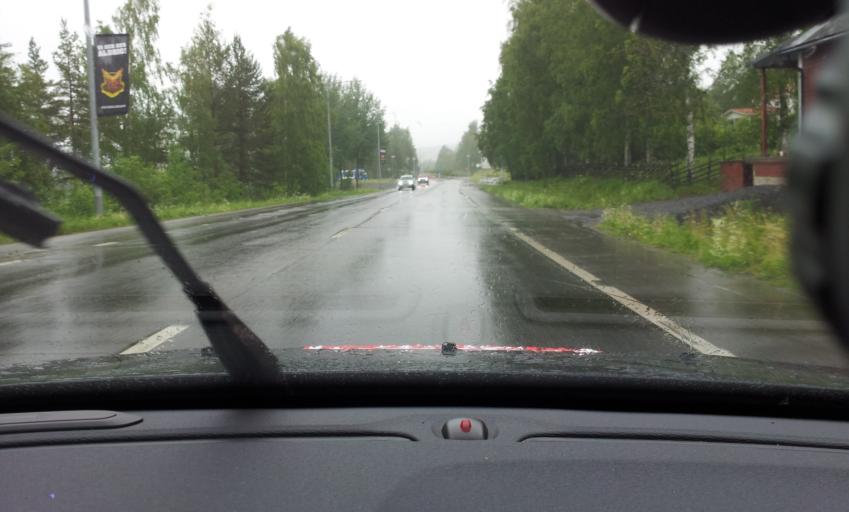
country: SE
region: Jaemtland
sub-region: OEstersunds Kommun
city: Ostersund
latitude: 63.1930
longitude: 14.6596
